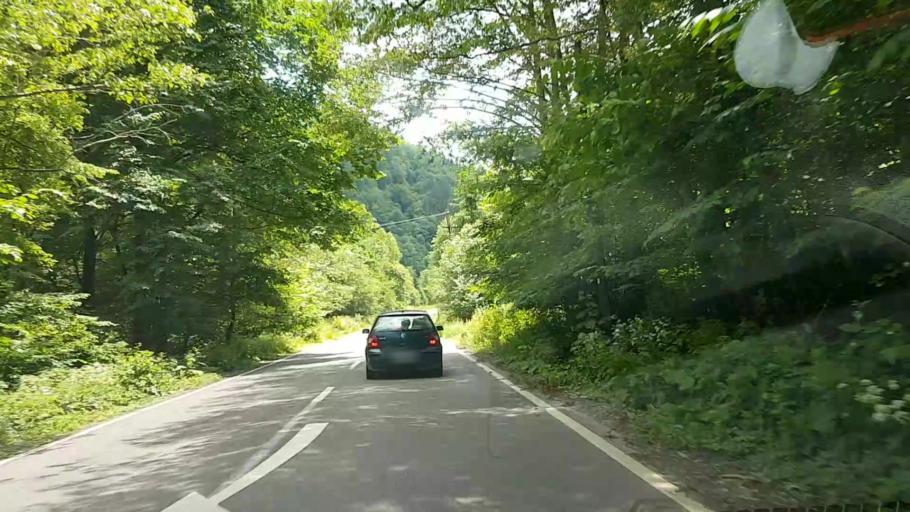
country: RO
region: Suceava
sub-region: Comuna Crucea
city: Crucea
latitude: 47.3012
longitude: 25.6303
